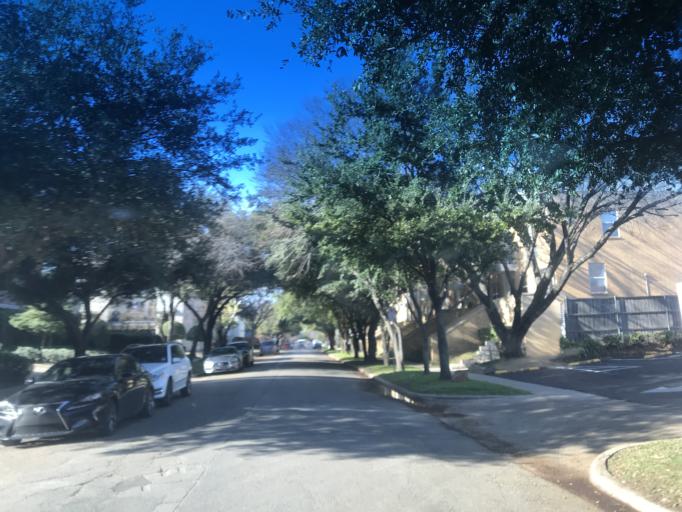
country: US
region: Texas
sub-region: Dallas County
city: Highland Park
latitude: 32.8153
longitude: -96.8041
